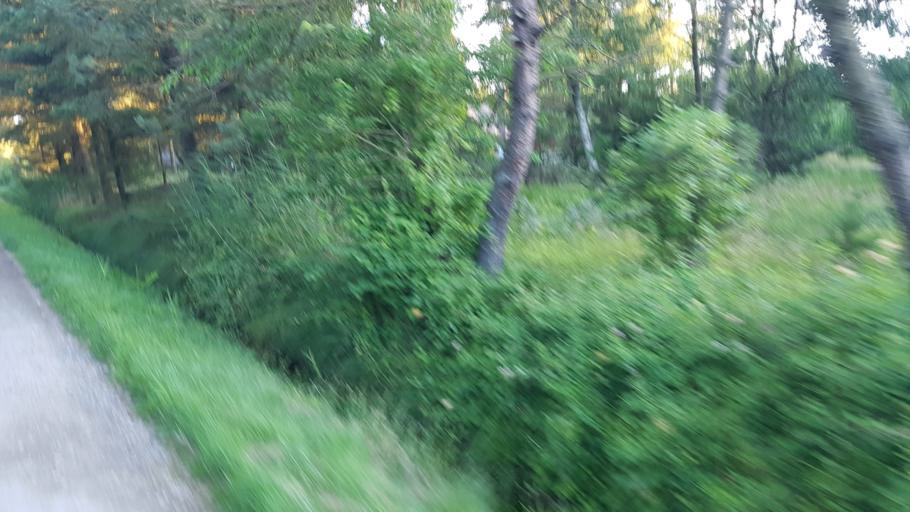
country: DE
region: Schleswig-Holstein
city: List
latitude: 55.0929
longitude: 8.5256
